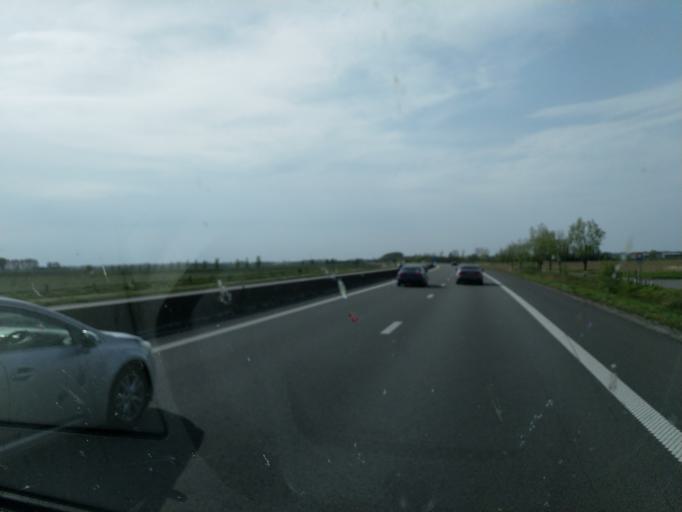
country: BE
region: Flanders
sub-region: Provincie West-Vlaanderen
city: Veurne
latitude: 51.0638
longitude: 2.6395
